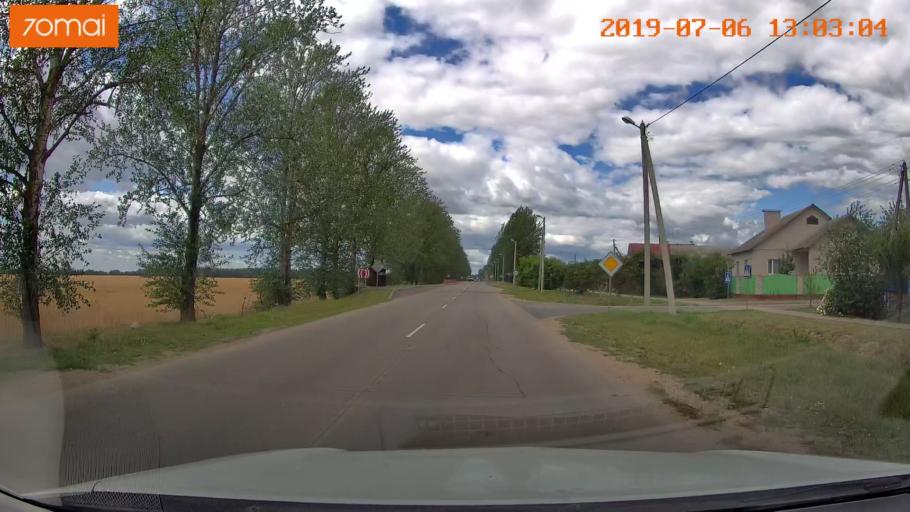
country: BY
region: Minsk
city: Dzyarzhynsk
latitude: 53.6880
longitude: 27.1072
